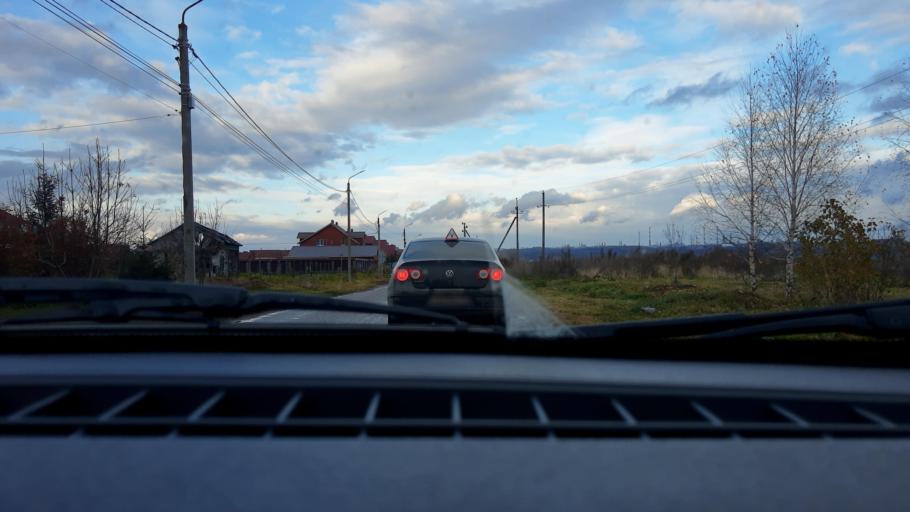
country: RU
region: Bashkortostan
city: Ufa
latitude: 54.8536
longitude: 56.0164
